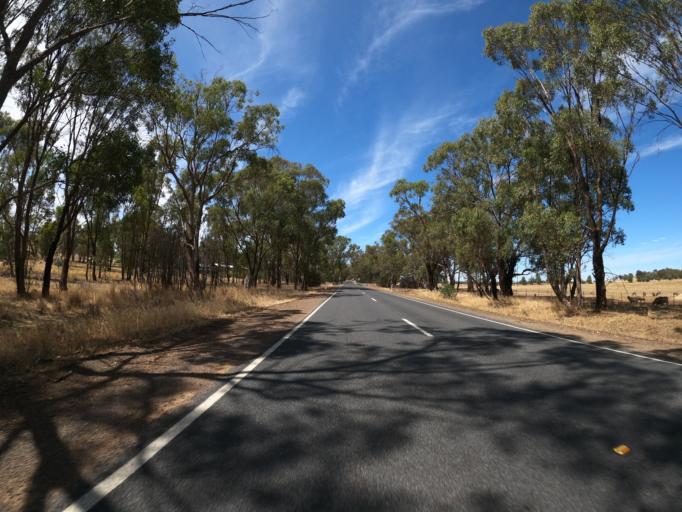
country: AU
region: Victoria
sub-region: Benalla
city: Benalla
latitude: -36.3938
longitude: 145.9807
